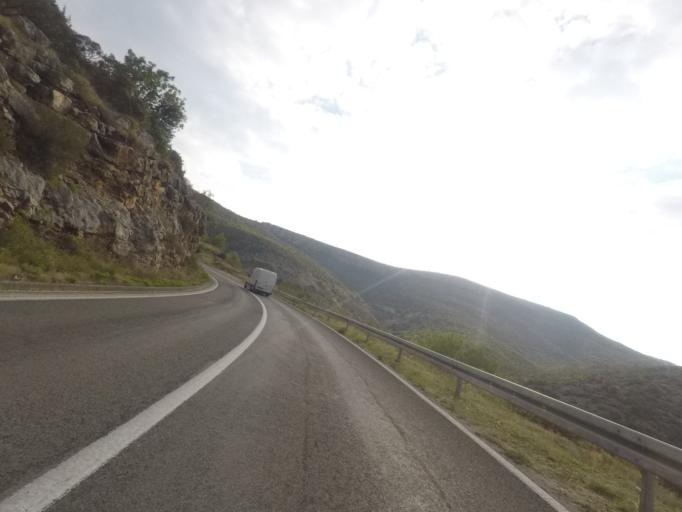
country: HR
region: Splitsko-Dalmatinska
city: Stari Grad
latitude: 43.1713
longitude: 16.5641
